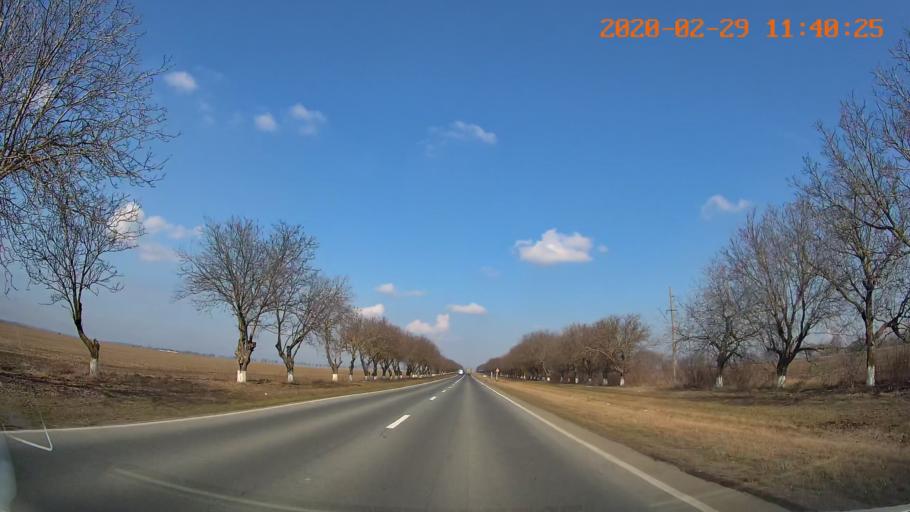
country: MD
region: Rezina
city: Saharna
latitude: 47.6560
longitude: 29.0203
